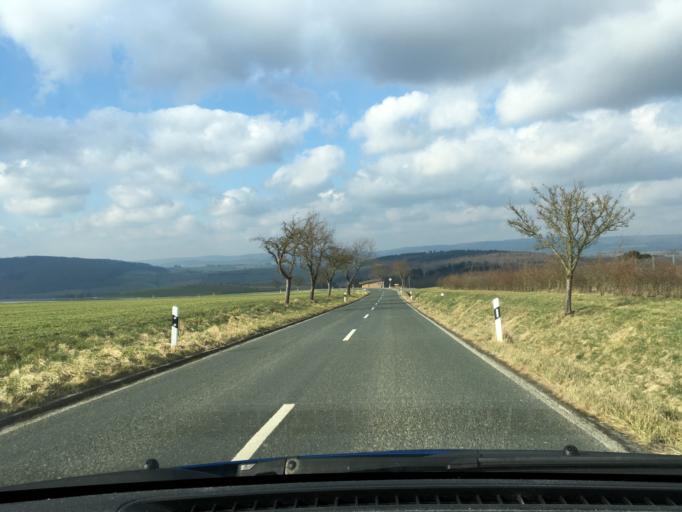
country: DE
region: Lower Saxony
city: Uslar
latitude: 51.6059
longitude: 9.6382
